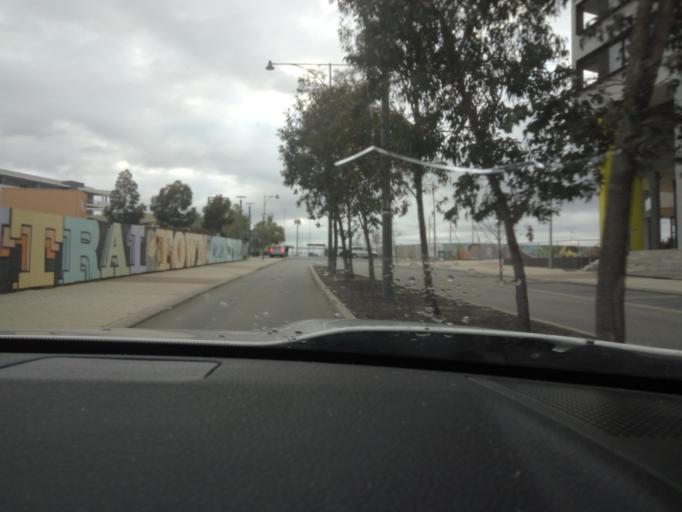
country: AU
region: Western Australia
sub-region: City of Cockburn
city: Success
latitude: -32.1263
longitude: 115.8562
